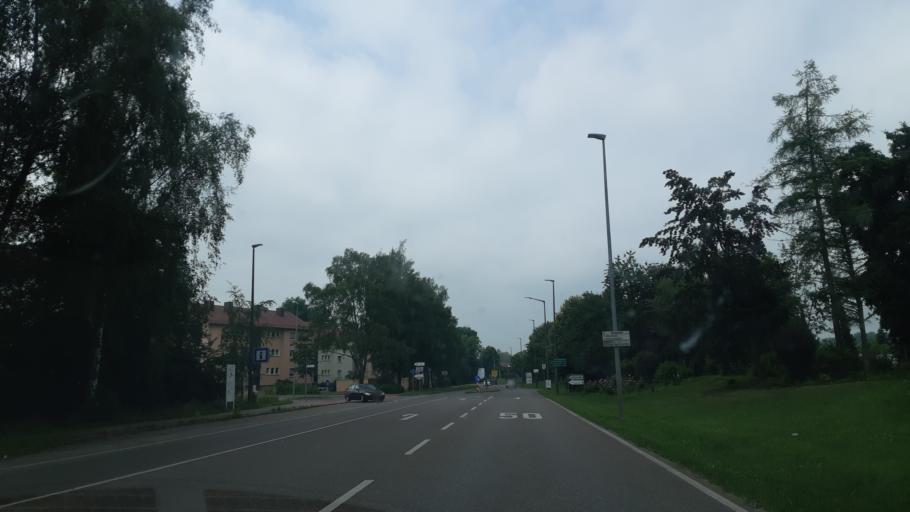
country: DE
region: Baden-Wuerttemberg
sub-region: Regierungsbezirk Stuttgart
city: Goeppingen
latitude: 48.6907
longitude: 9.6302
